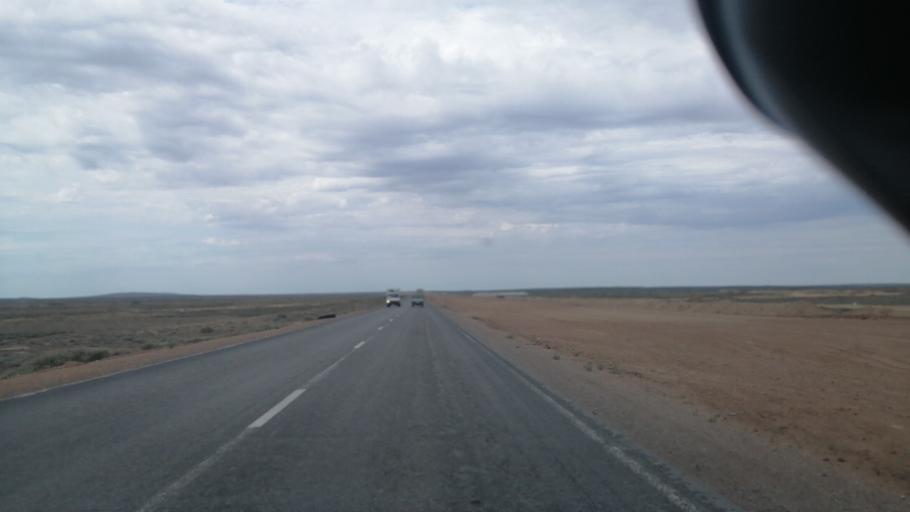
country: KZ
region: Qaraghandy
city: Saryshaghan
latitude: 46.4832
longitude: 74.0565
